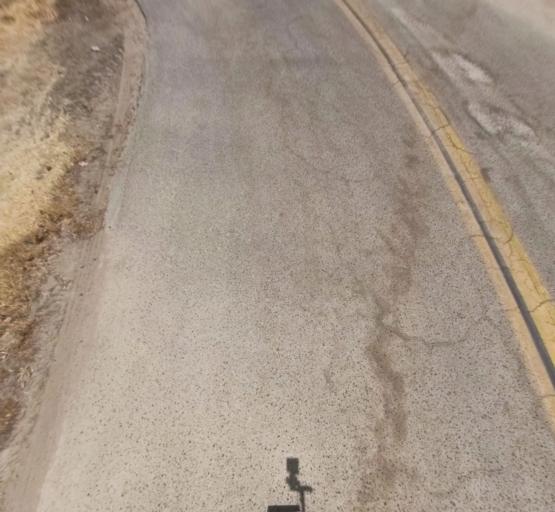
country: US
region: California
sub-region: Fresno County
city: Kerman
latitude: 36.8258
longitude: -120.2112
